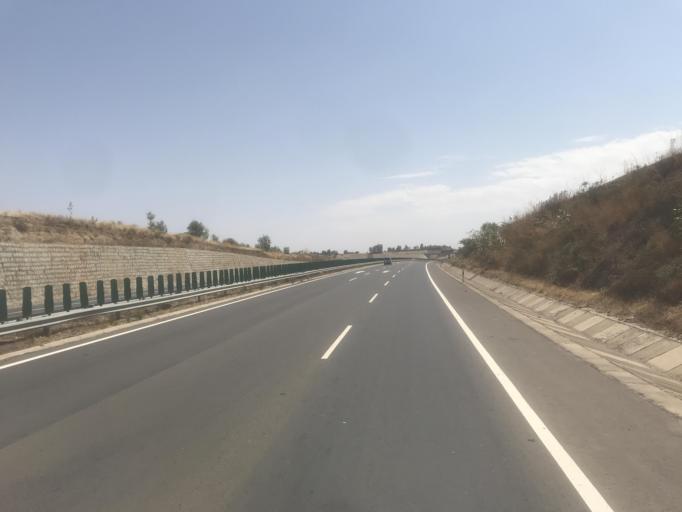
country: ET
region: Oromiya
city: Mojo
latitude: 8.5832
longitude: 39.1680
